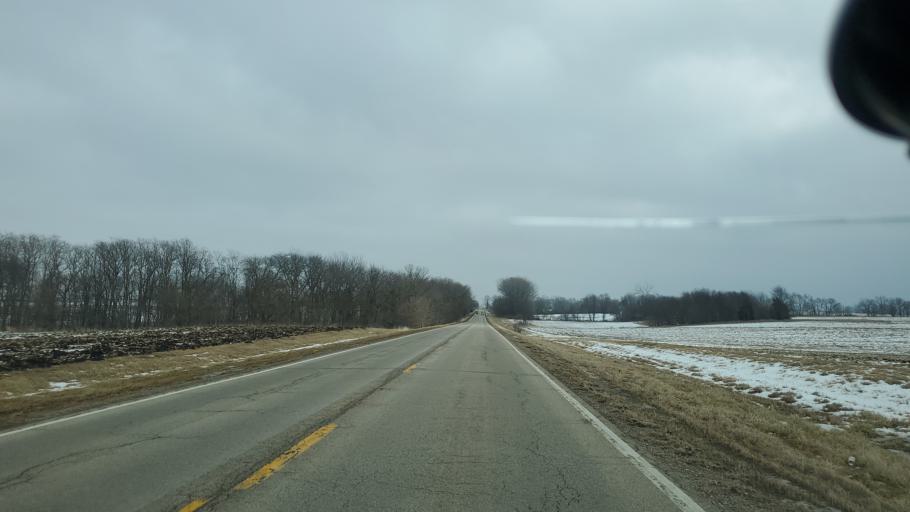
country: US
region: Illinois
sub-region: Marshall County
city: Toluca
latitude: 41.1187
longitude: -89.1620
